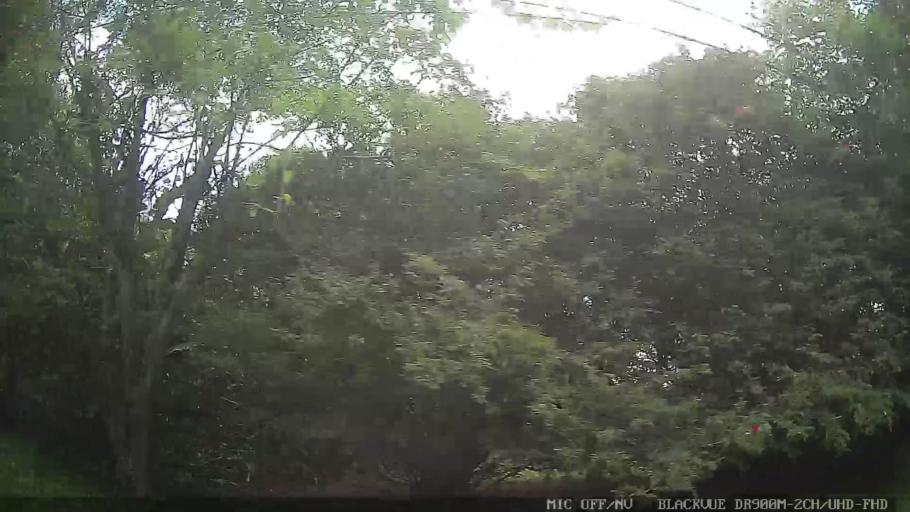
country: BR
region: Sao Paulo
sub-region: Aruja
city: Aruja
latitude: -23.4170
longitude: -46.3393
